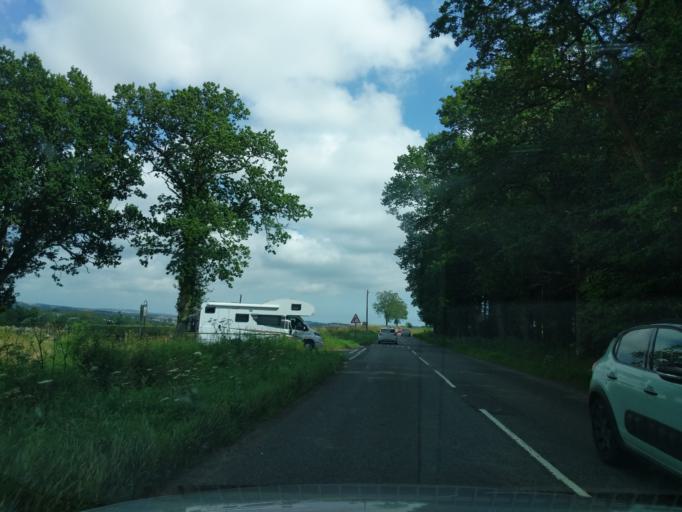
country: GB
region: Scotland
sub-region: Angus
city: Muirhead
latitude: 56.5042
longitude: -3.1244
